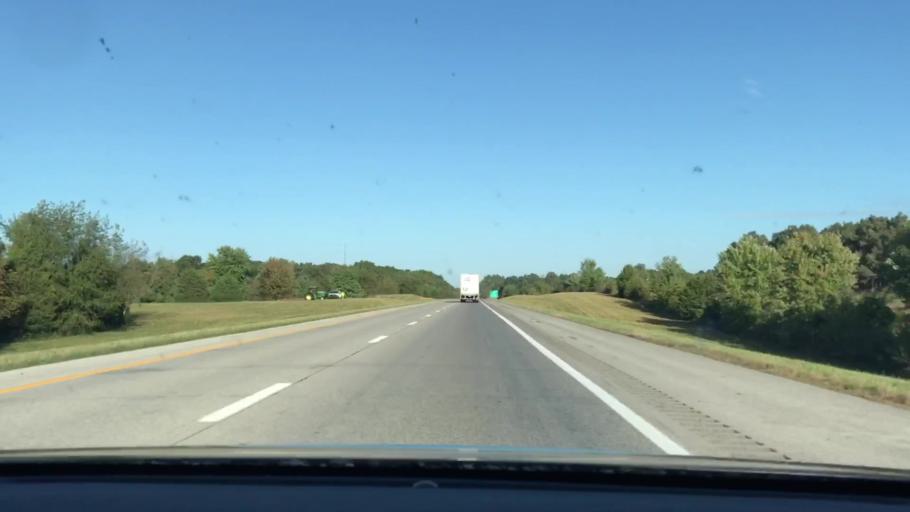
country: US
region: Kentucky
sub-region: Trigg County
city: Cadiz
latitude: 36.9450
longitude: -87.8340
